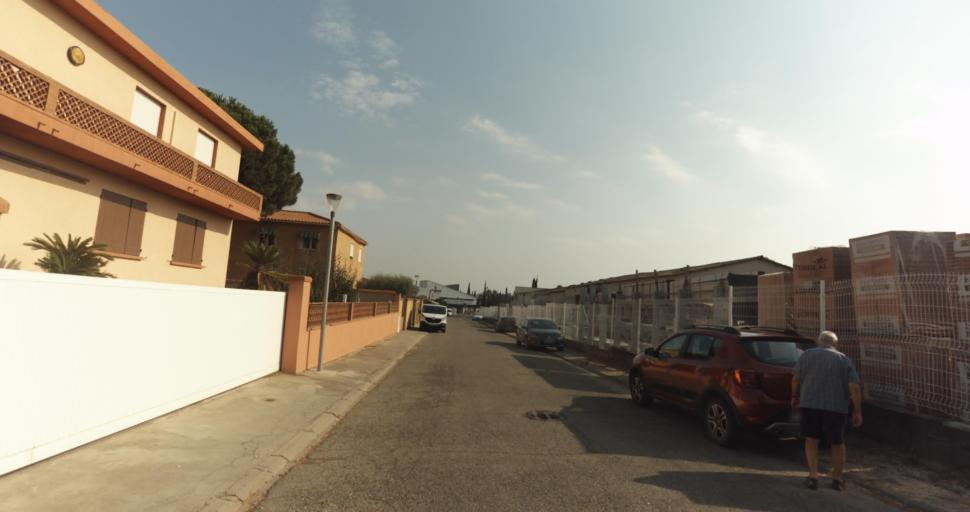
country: FR
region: Languedoc-Roussillon
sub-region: Departement des Pyrenees-Orientales
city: Latour-Bas-Elne
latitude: 42.6157
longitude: 2.9966
